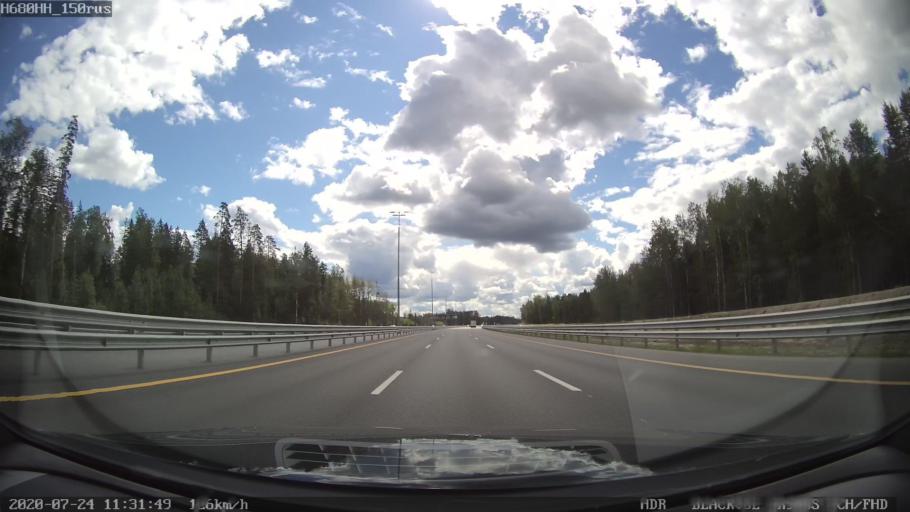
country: RU
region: Leningrad
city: Krasnyy Bor
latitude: 59.6511
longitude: 30.6460
